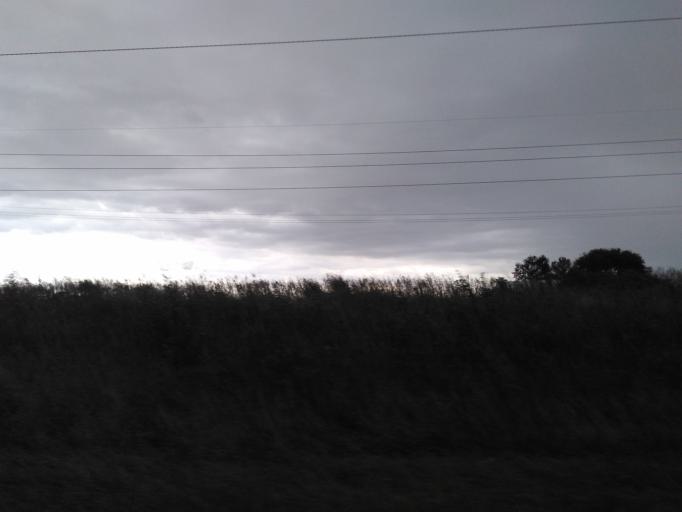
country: US
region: Illinois
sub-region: Madison County
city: Highland
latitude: 38.7370
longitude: -89.7050
